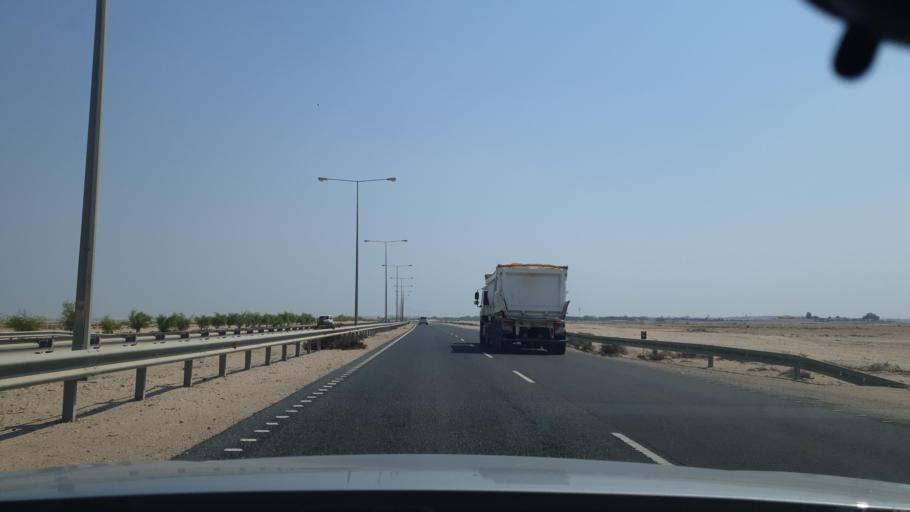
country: QA
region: Al Khawr
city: Al Khawr
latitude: 25.7424
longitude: 51.4850
